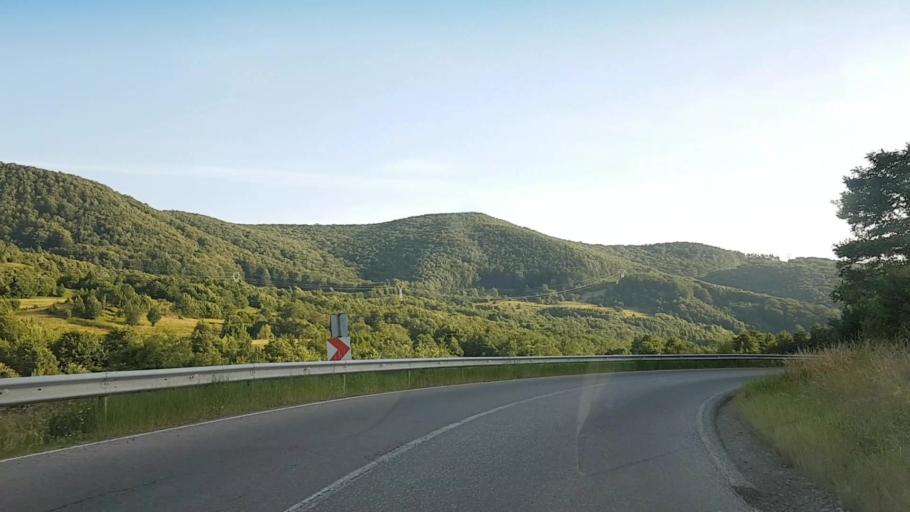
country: RO
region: Harghita
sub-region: Comuna Praid
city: Praid
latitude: 46.5675
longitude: 25.1635
